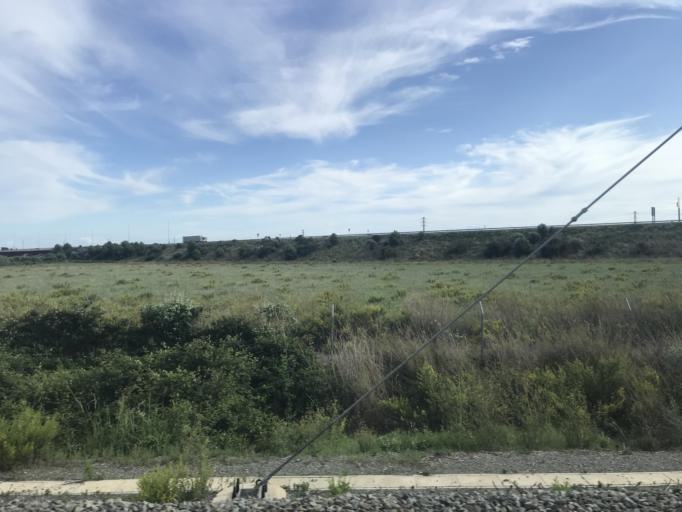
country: ES
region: Catalonia
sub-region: Provincia de Tarragona
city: Cambrils
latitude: 41.0865
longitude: 1.0626
